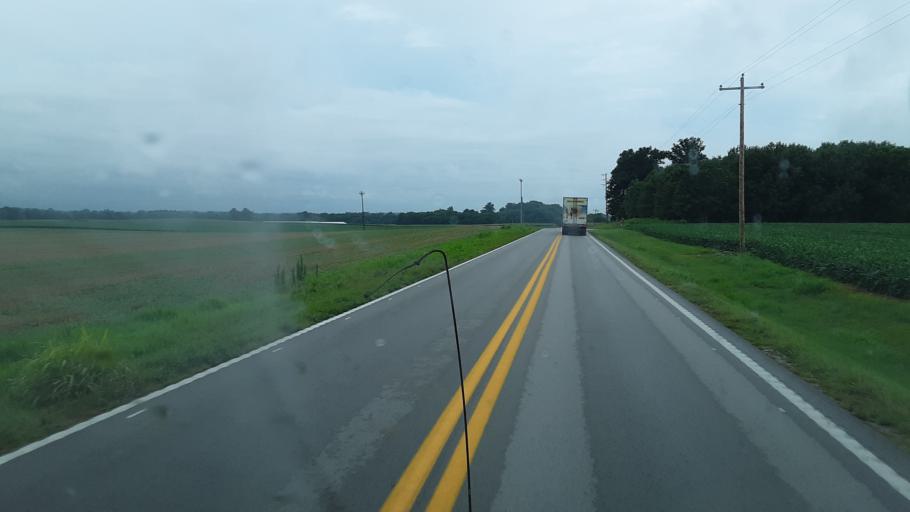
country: US
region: Kentucky
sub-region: Todd County
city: Elkton
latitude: 36.7372
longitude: -87.0670
